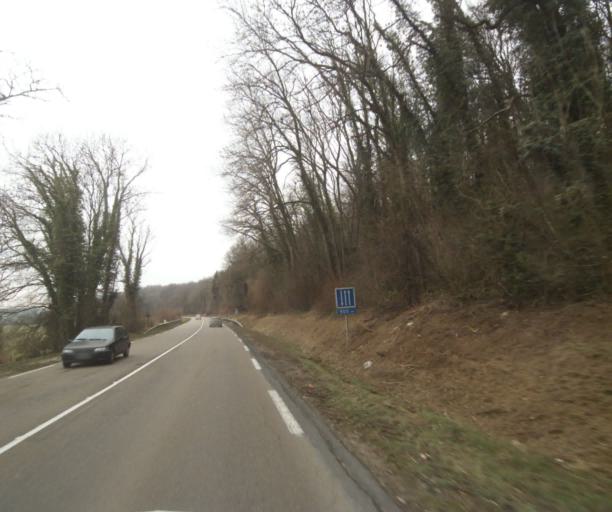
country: FR
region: Champagne-Ardenne
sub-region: Departement de la Haute-Marne
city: Bienville
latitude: 48.5987
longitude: 5.0323
